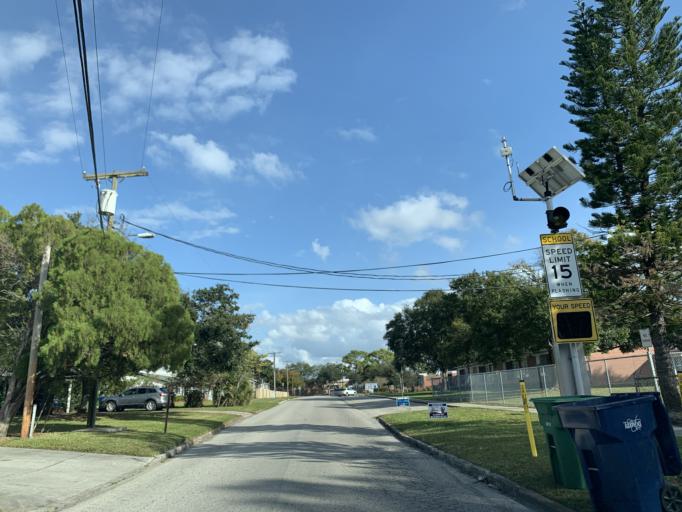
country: US
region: Florida
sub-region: Hillsborough County
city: Tampa
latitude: 27.9006
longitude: -82.5104
